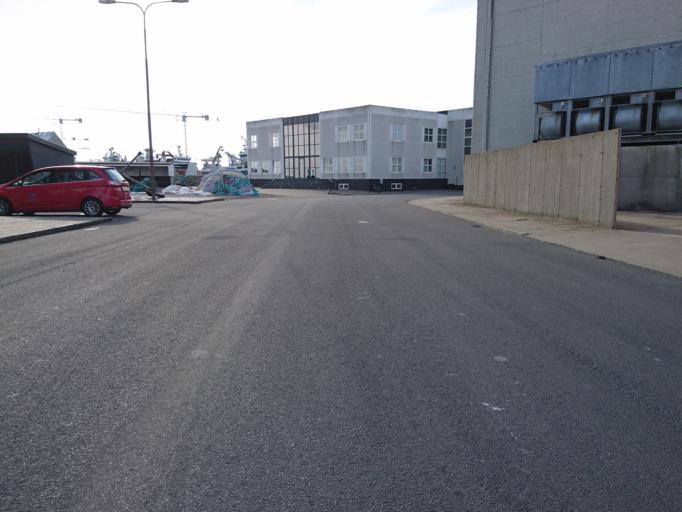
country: DK
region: North Denmark
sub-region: Frederikshavn Kommune
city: Skagen
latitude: 57.7170
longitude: 10.5953
